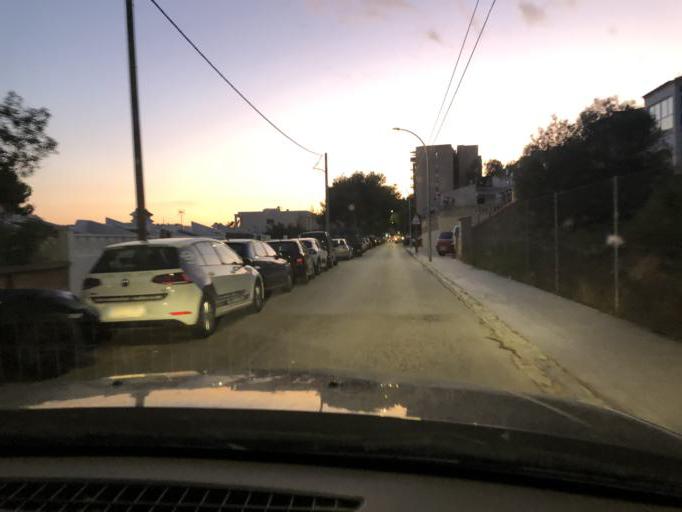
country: ES
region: Balearic Islands
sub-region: Illes Balears
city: Santa Ponsa
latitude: 39.5214
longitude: 2.4871
